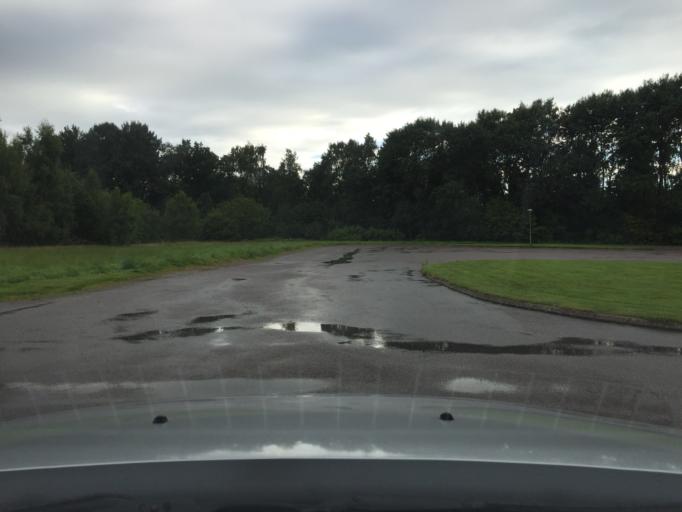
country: SE
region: Skane
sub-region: Hoors Kommun
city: Hoeoer
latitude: 55.9505
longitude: 13.5627
